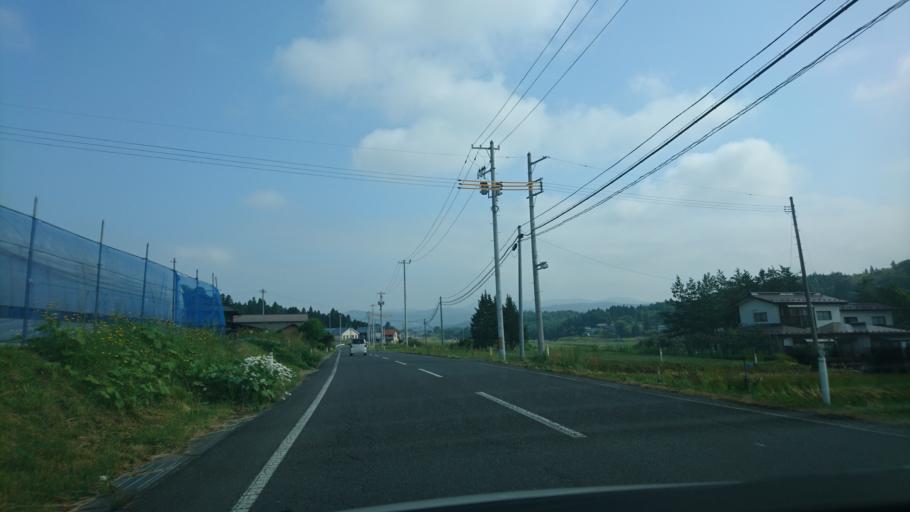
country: JP
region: Iwate
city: Ichinoseki
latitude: 38.9263
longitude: 141.1726
